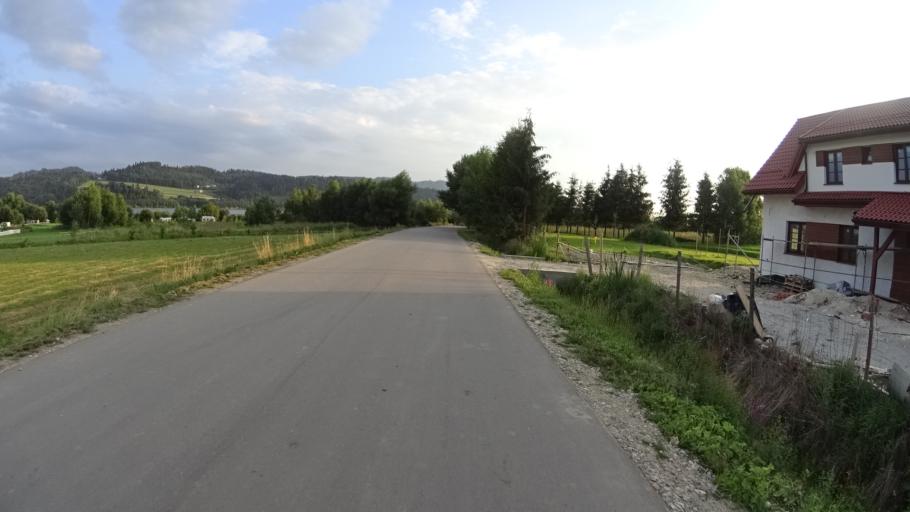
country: PL
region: Lesser Poland Voivodeship
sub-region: Powiat nowotarski
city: Maniowy
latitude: 49.4464
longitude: 20.2748
